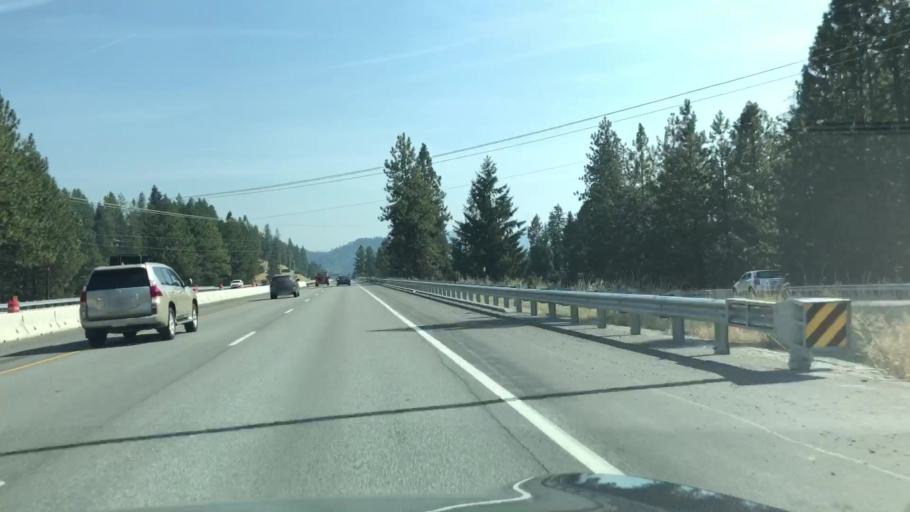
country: US
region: Idaho
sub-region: Kootenai County
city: Coeur d'Alene
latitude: 47.6899
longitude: -116.7662
